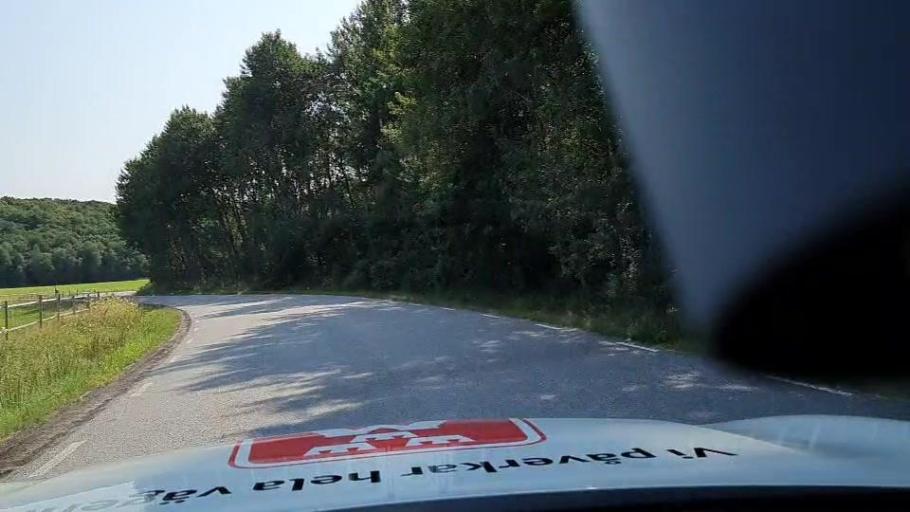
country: SE
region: Vaestra Goetaland
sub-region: Tjorns Kommun
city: Skaerhamn
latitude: 58.1208
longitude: 11.5373
